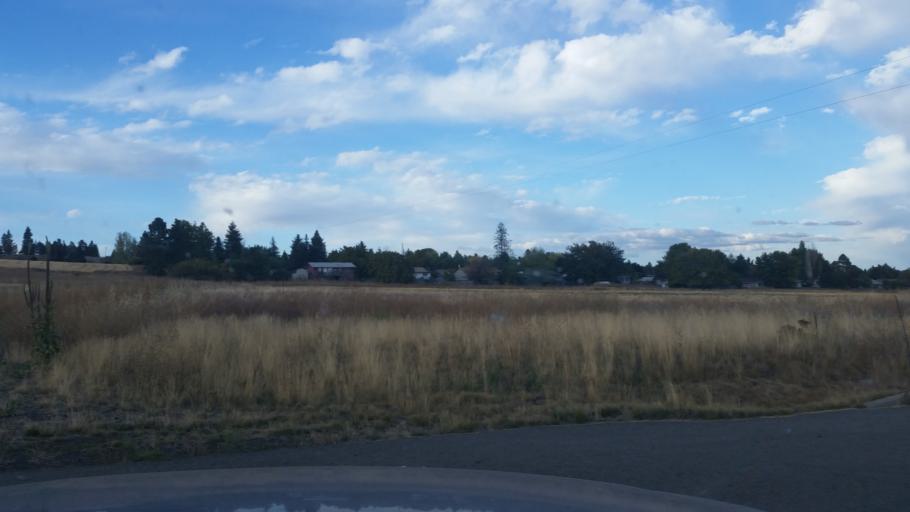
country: US
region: Washington
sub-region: Spokane County
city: Cheney
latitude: 47.4768
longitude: -117.6025
